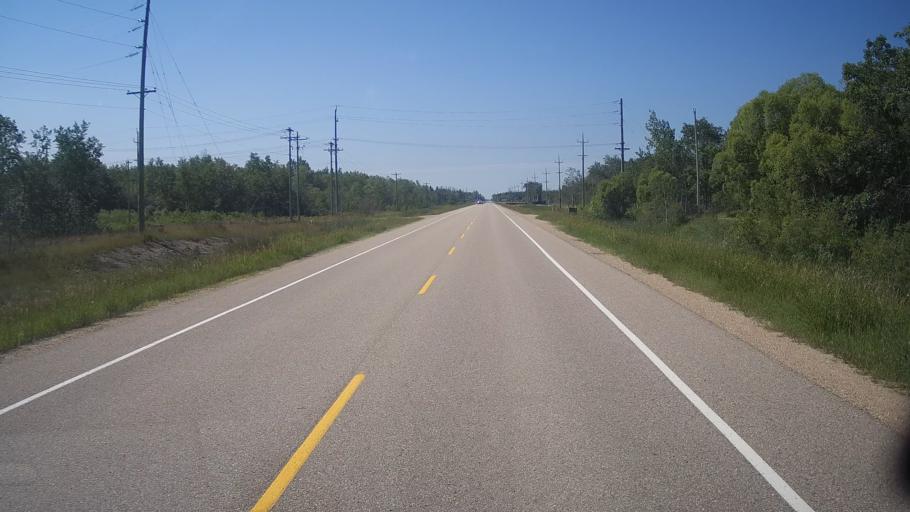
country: CA
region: Manitoba
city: La Broquerie
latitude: 49.6717
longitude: -96.4569
